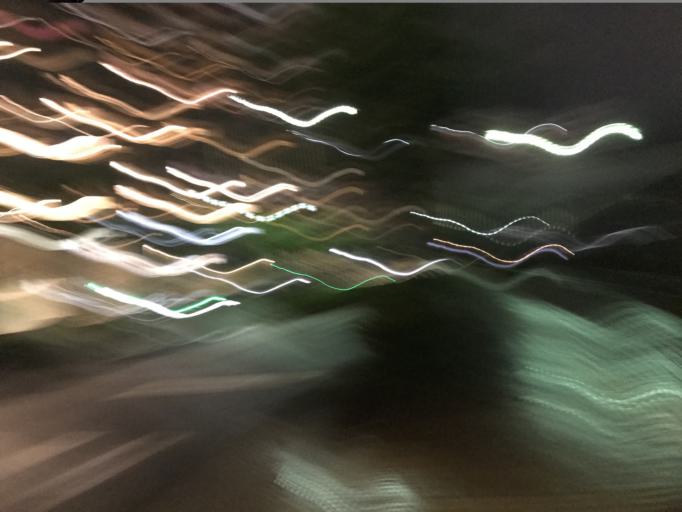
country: JP
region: Shiga Prefecture
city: Otsu-shi
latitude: 35.0130
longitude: 135.8644
